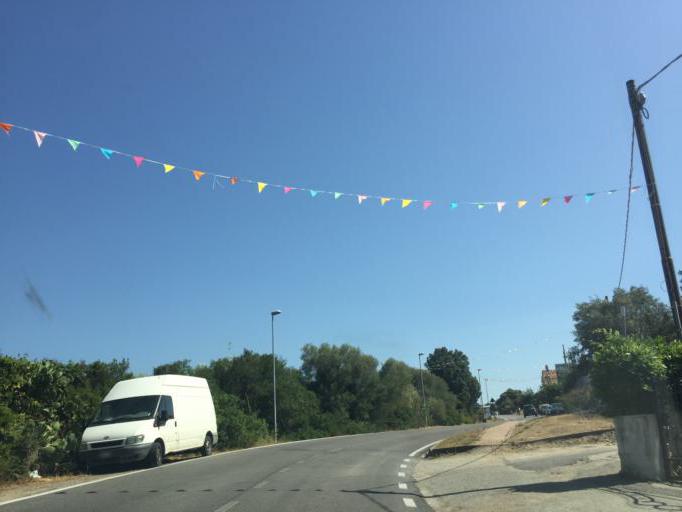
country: IT
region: Sardinia
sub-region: Provincia di Olbia-Tempio
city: San Teodoro
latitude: 40.7503
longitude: 9.6472
